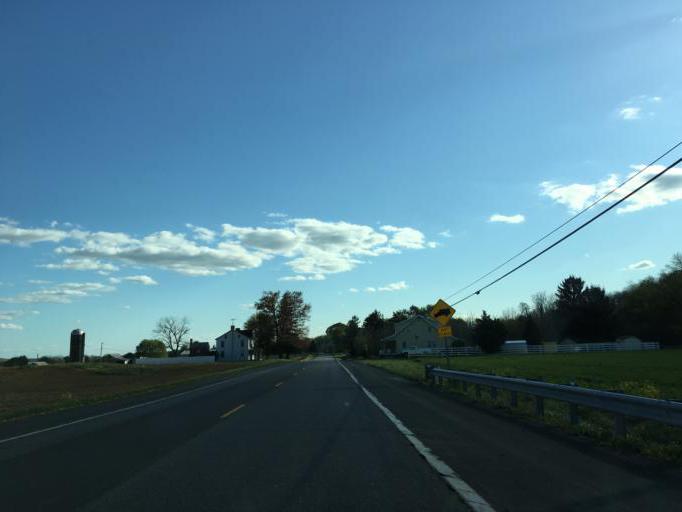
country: US
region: Maryland
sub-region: Frederick County
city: Woodsboro
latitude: 39.5567
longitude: -77.3029
